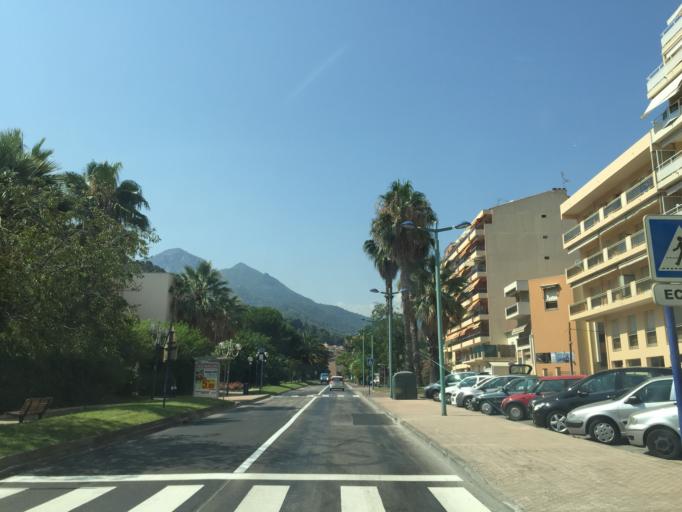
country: FR
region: Provence-Alpes-Cote d'Azur
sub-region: Departement des Alpes-Maritimes
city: Menton
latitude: 43.7860
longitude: 7.4945
